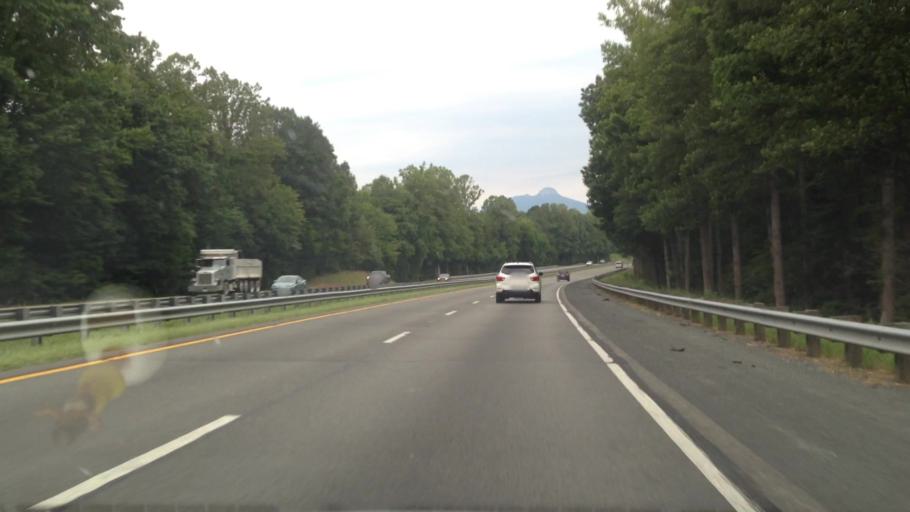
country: US
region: North Carolina
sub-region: Stokes County
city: King
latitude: 36.2871
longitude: -80.3988
